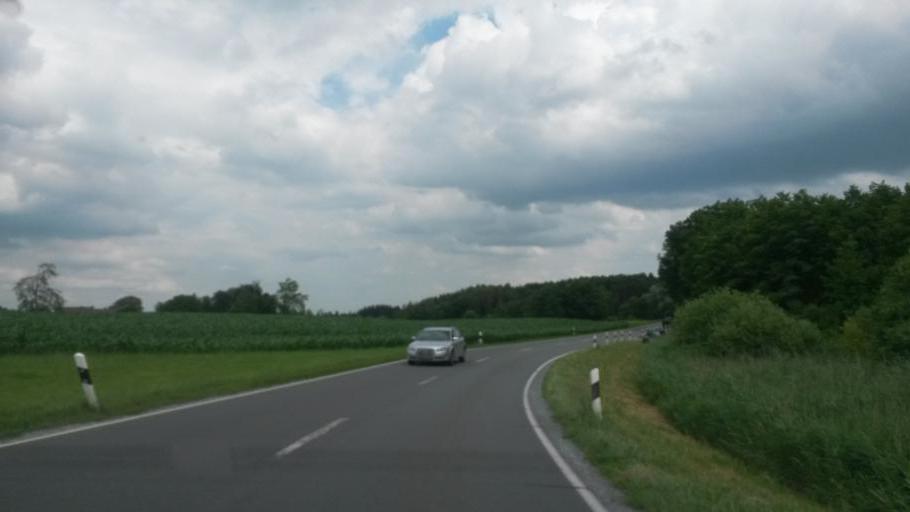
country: DE
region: Bavaria
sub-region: Upper Bavaria
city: Eggstatt
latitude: 47.9372
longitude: 12.3679
